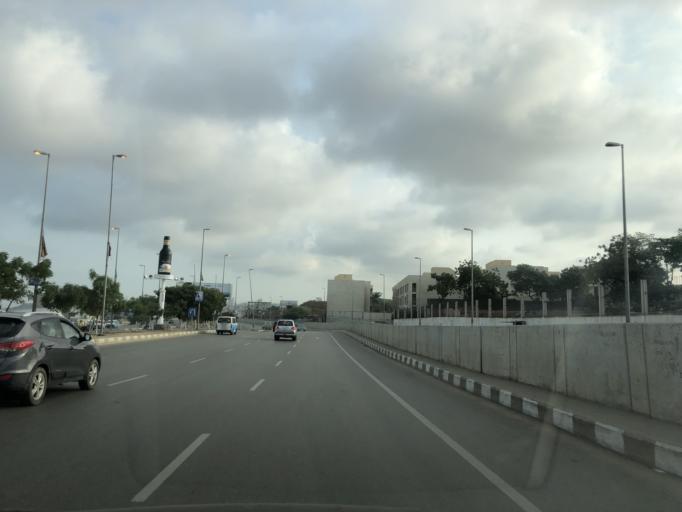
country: AO
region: Luanda
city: Luanda
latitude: -8.8690
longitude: 13.2126
